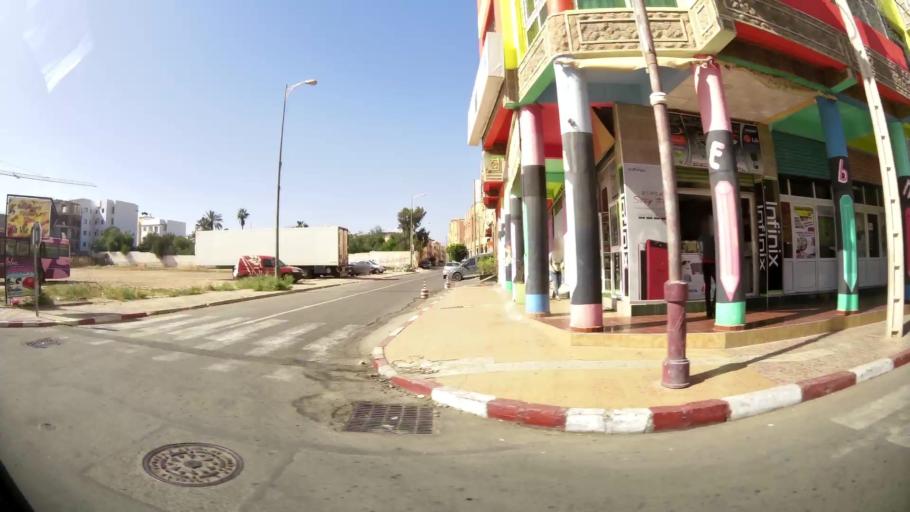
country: MA
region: Souss-Massa-Draa
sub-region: Inezgane-Ait Mellou
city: Inezgane
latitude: 30.3719
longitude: -9.5458
